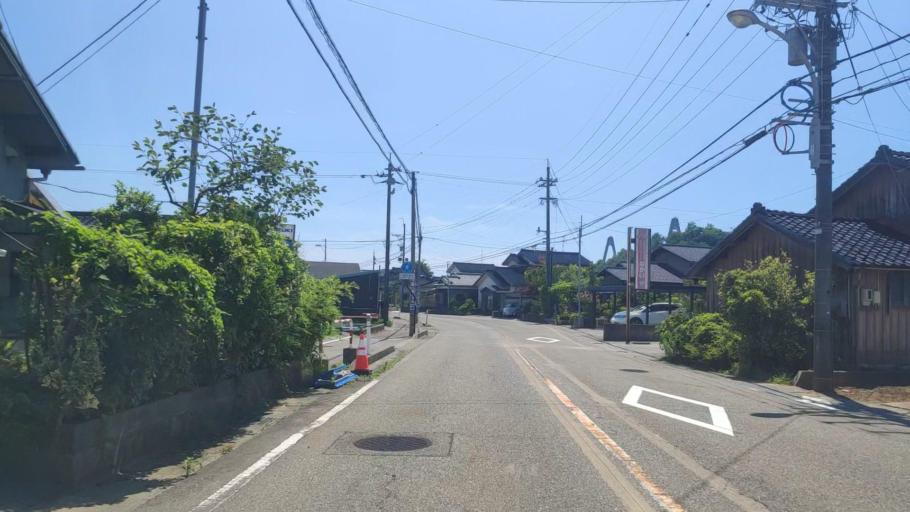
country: JP
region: Ishikawa
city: Kanazawa-shi
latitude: 36.6643
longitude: 136.6576
